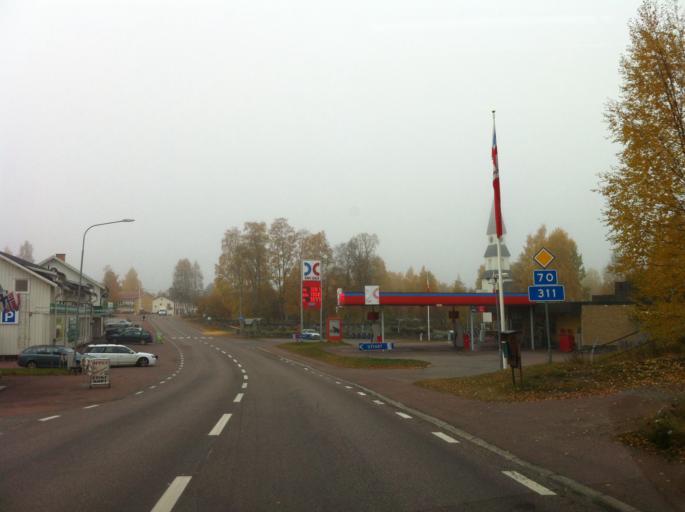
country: NO
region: Hedmark
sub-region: Trysil
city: Innbygda
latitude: 61.6929
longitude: 13.1426
